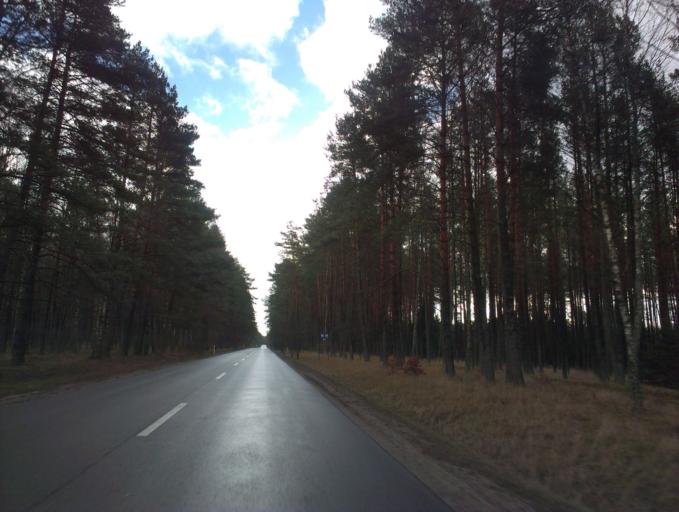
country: PL
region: Pomeranian Voivodeship
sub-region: Powiat czluchowski
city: Czarne
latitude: 53.6987
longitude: 16.8879
